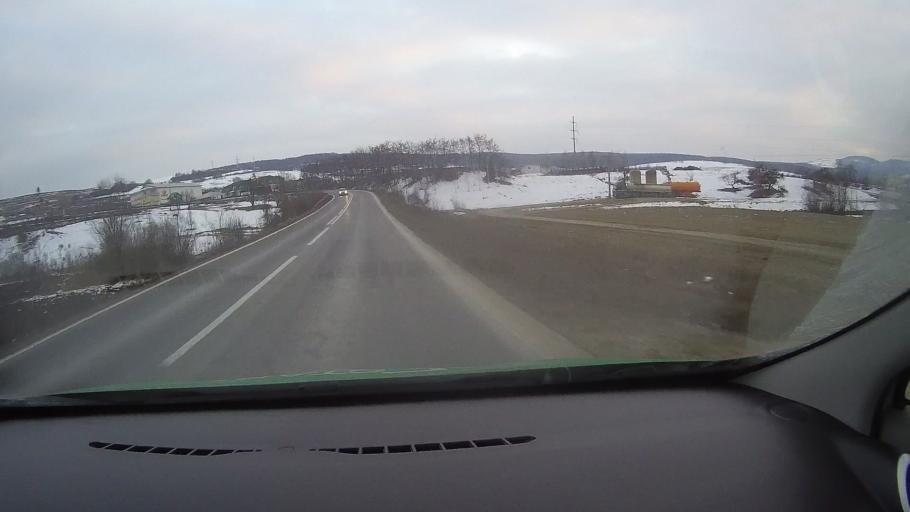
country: RO
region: Harghita
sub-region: Comuna Lupeni
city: Lupeni
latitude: 46.3572
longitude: 25.2390
